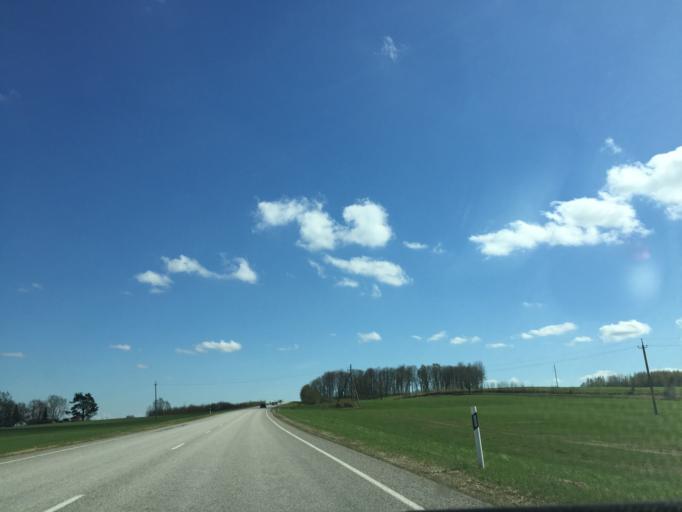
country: EE
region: Valgamaa
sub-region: Valga linn
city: Valga
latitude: 57.9079
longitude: 26.0431
